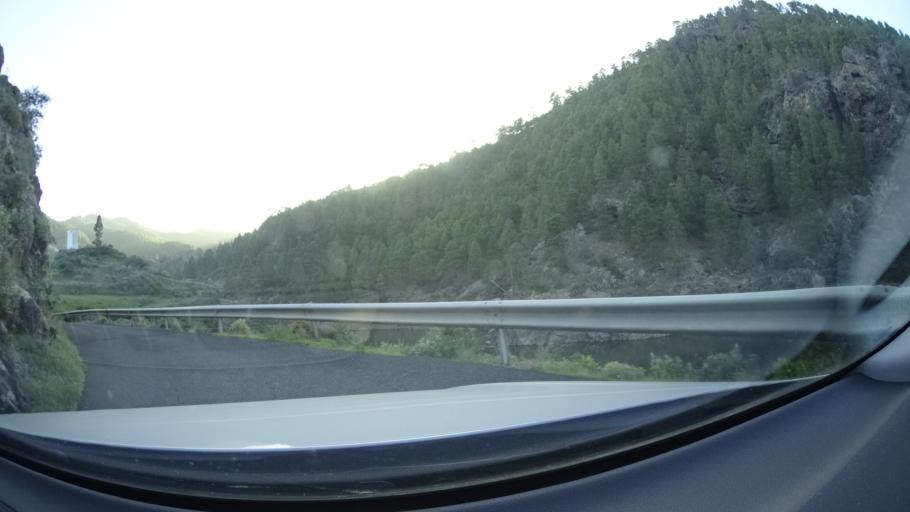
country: ES
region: Canary Islands
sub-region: Provincia de Las Palmas
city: Artenara
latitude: 28.0435
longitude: -15.6745
